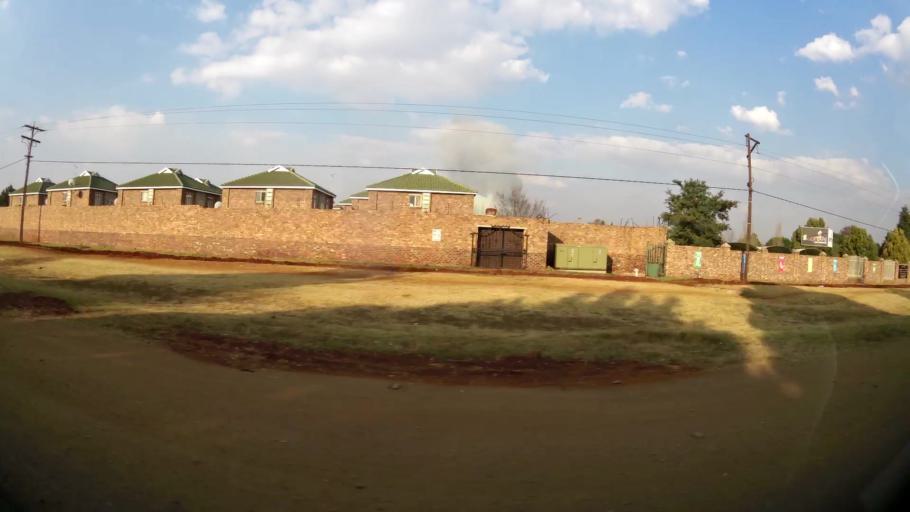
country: ZA
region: Gauteng
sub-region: Ekurhuleni Metropolitan Municipality
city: Benoni
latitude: -26.1115
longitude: 28.2952
